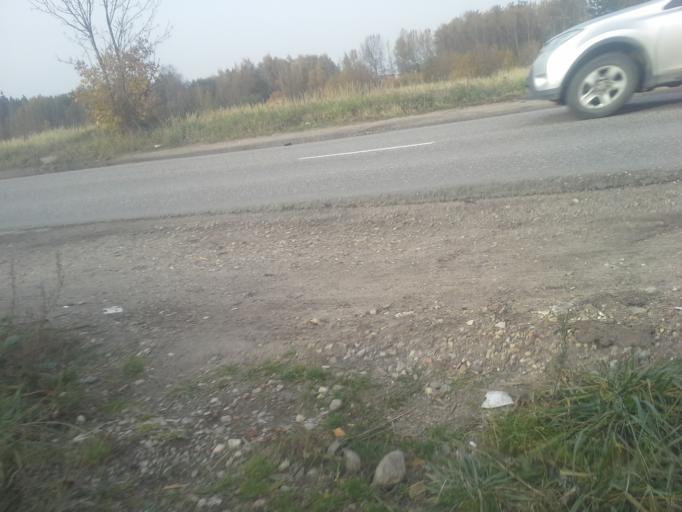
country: RU
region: Moskovskaya
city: Krasnoznamensk
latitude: 55.5936
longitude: 37.0181
